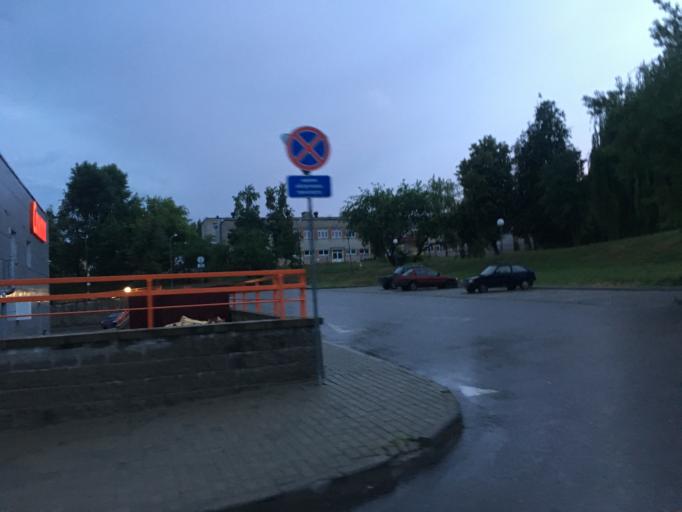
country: BY
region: Grodnenskaya
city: Hrodna
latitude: 53.6978
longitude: 23.8280
